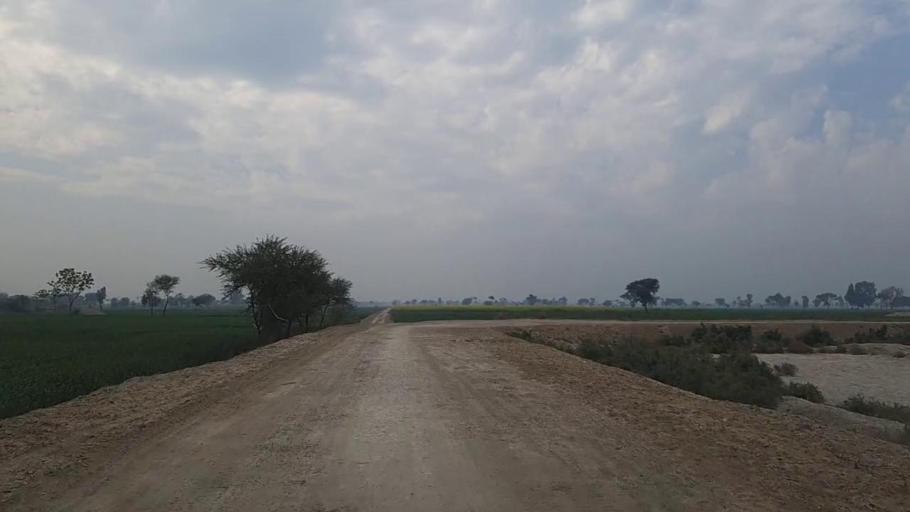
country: PK
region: Sindh
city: Daur
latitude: 26.3654
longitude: 68.3903
